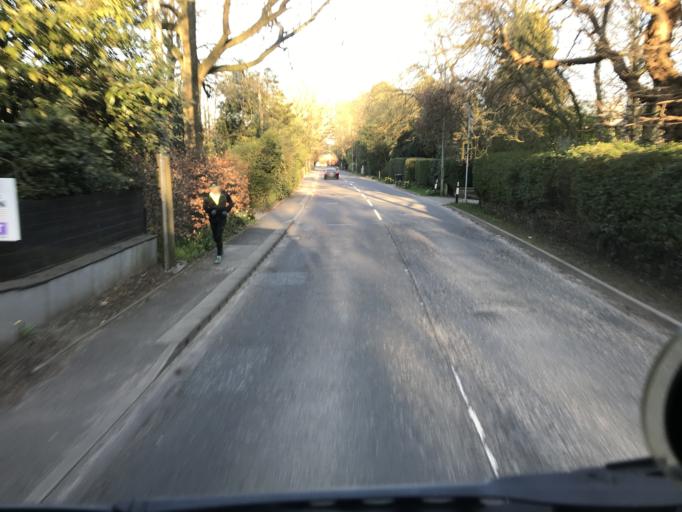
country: GB
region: England
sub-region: Cheshire East
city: Wilmslow
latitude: 53.3282
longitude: -2.2081
